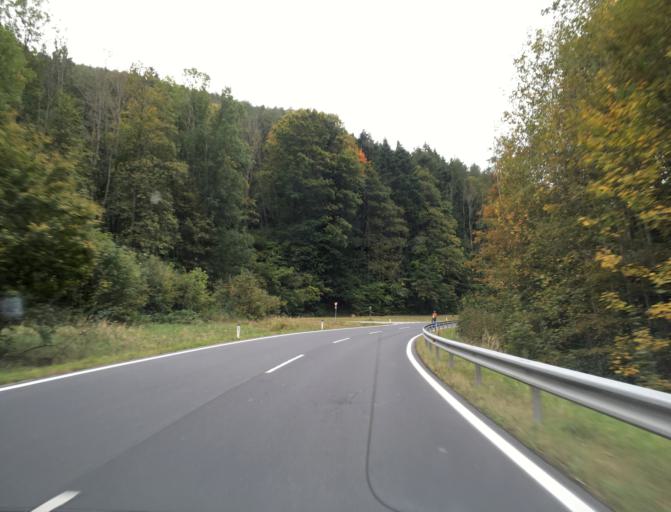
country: AT
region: Lower Austria
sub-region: Politischer Bezirk Neunkirchen
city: Edlitz
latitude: 47.5831
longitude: 16.1454
